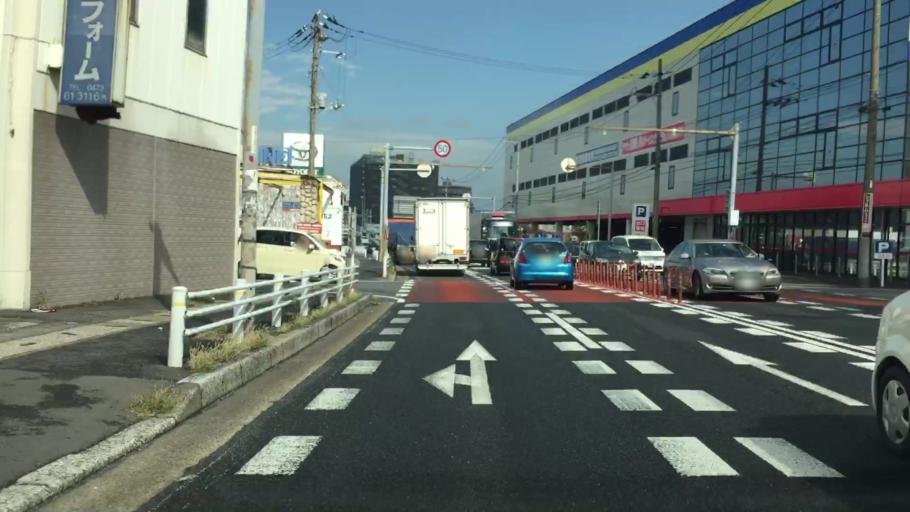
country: JP
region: Chiba
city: Matsudo
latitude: 35.7786
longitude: 139.9085
